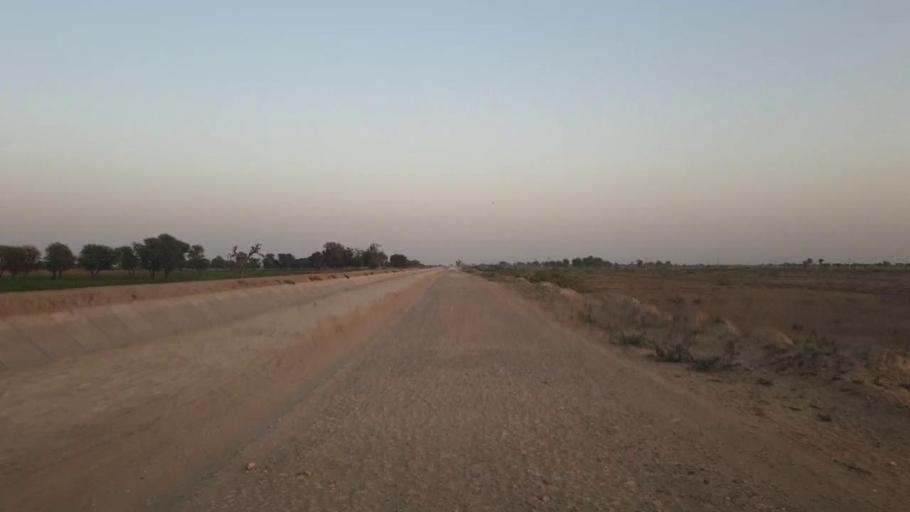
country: PK
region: Sindh
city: Dhoro Naro
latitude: 25.4511
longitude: 69.6215
